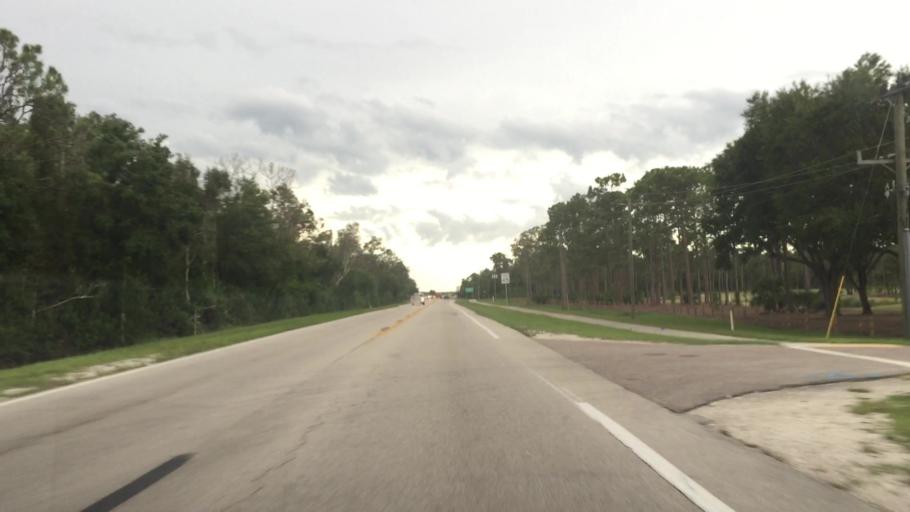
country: US
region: Florida
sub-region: Lee County
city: Fort Myers
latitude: 26.6230
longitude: -81.8116
